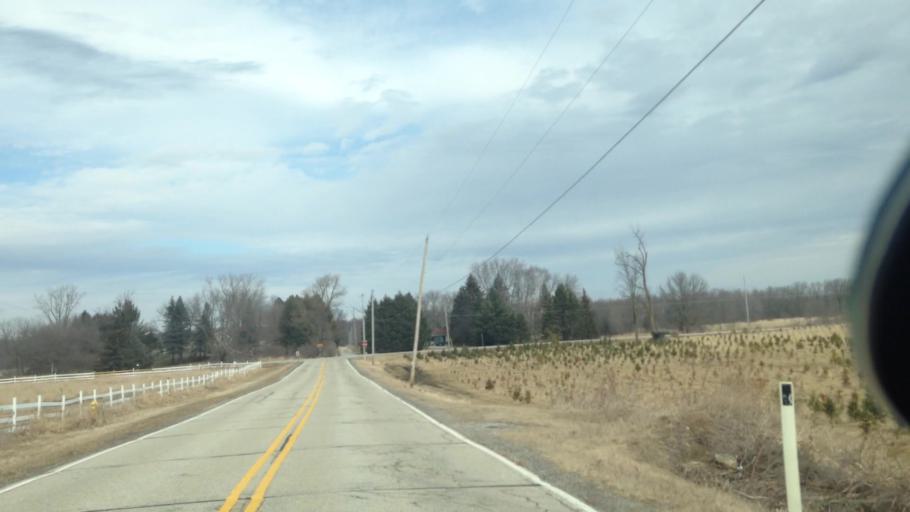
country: US
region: Wisconsin
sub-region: Waukesha County
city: Sussex
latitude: 43.1612
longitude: -88.2233
